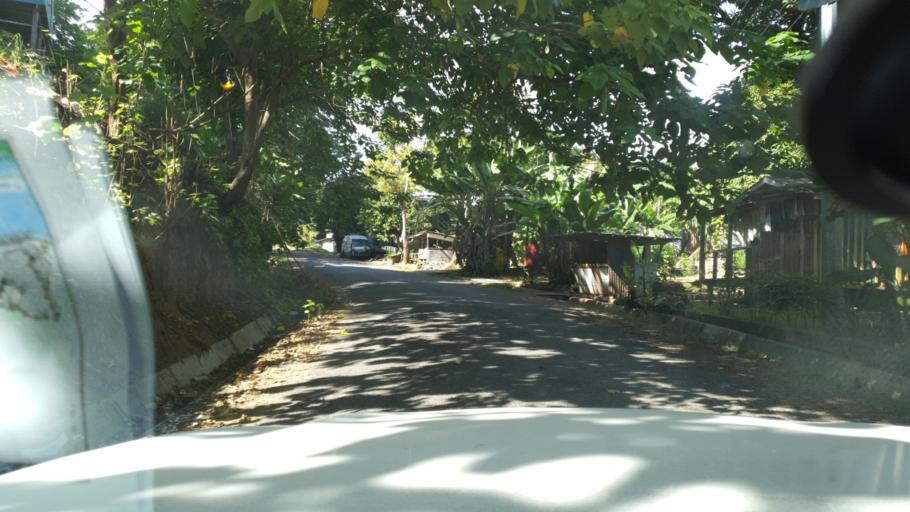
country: SB
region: Guadalcanal
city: Honiara
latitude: -9.4358
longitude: 159.9523
